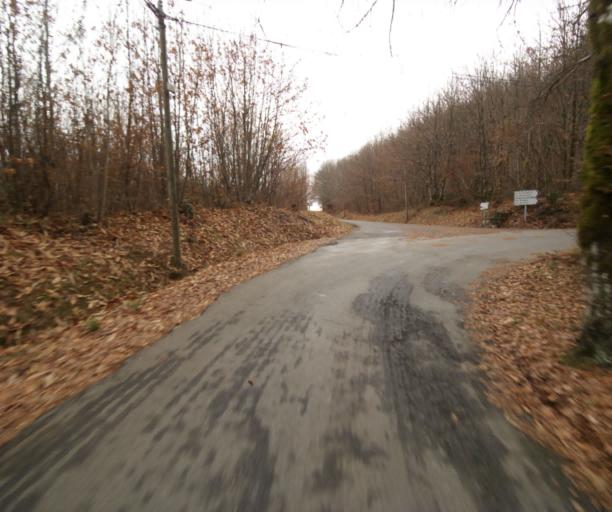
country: FR
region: Limousin
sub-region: Departement de la Correze
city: Chameyrat
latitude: 45.2348
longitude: 1.6881
